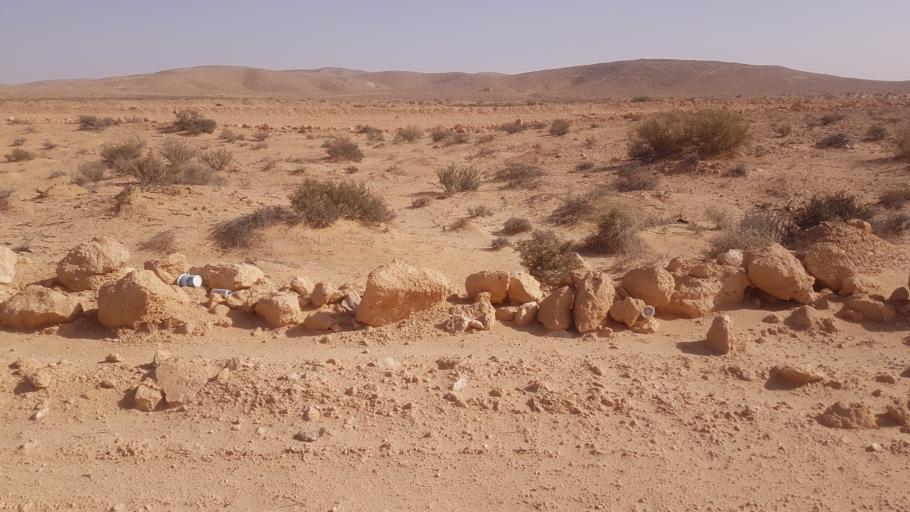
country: TN
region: Qabis
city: Matmata
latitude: 33.5933
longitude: 9.6978
